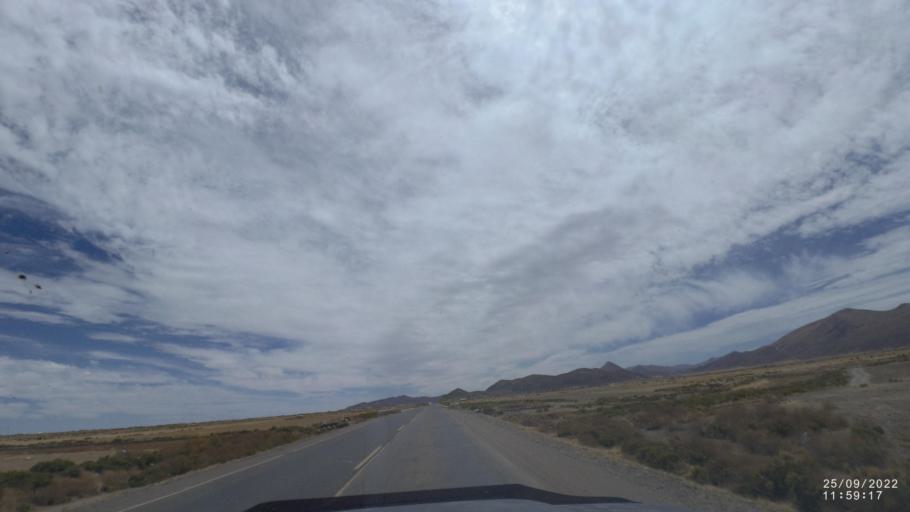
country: BO
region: Oruro
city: Challapata
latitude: -18.7902
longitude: -66.8456
